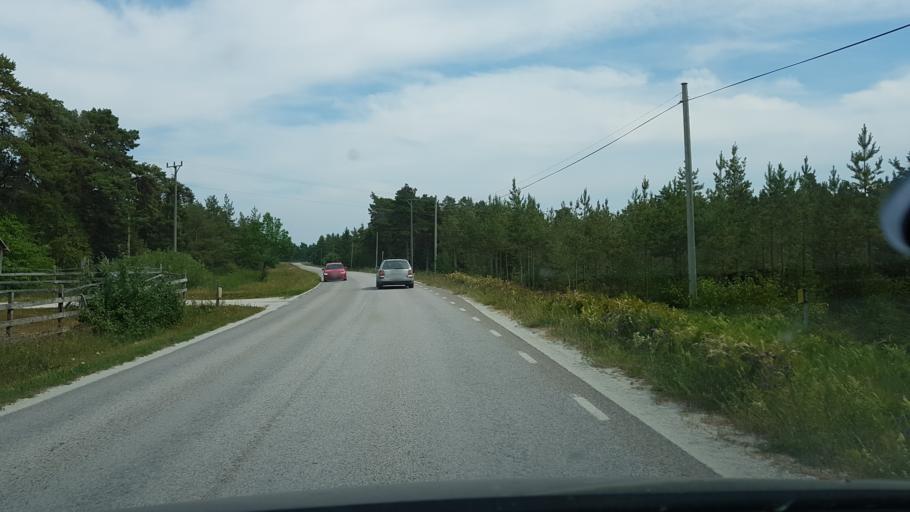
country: SE
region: Gotland
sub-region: Gotland
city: Slite
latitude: 57.7228
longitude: 18.7638
